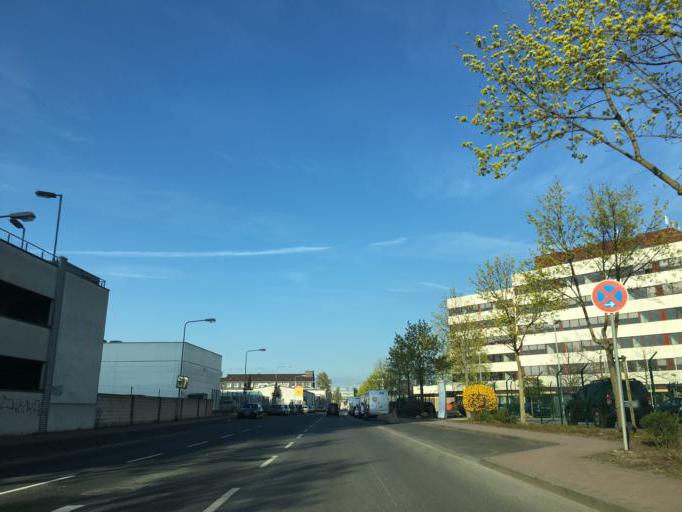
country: DE
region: Hesse
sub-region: Regierungsbezirk Darmstadt
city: Offenbach
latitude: 50.1218
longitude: 8.7413
